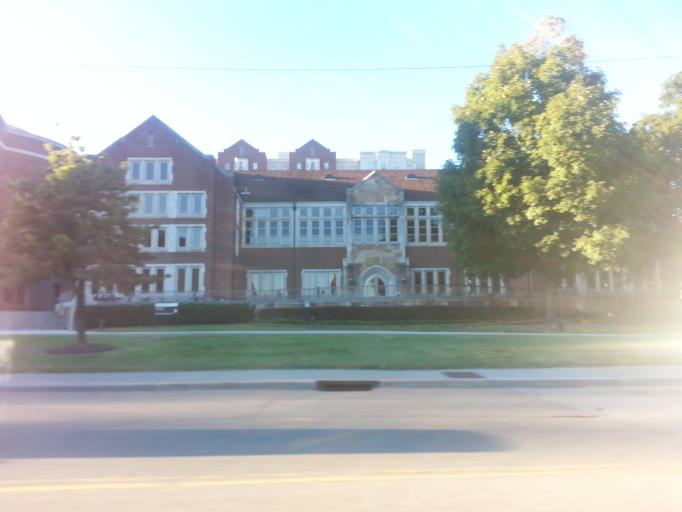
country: US
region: Tennessee
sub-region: Knox County
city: Knoxville
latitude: 35.9578
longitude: -83.9290
